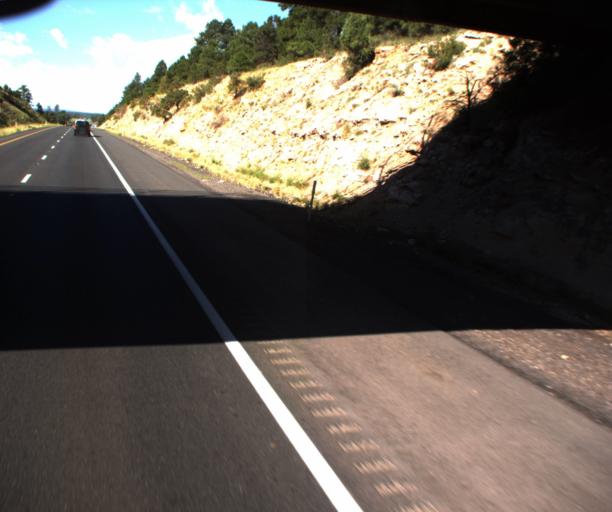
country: US
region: Arizona
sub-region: Coconino County
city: Flagstaff
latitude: 35.2022
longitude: -111.6084
